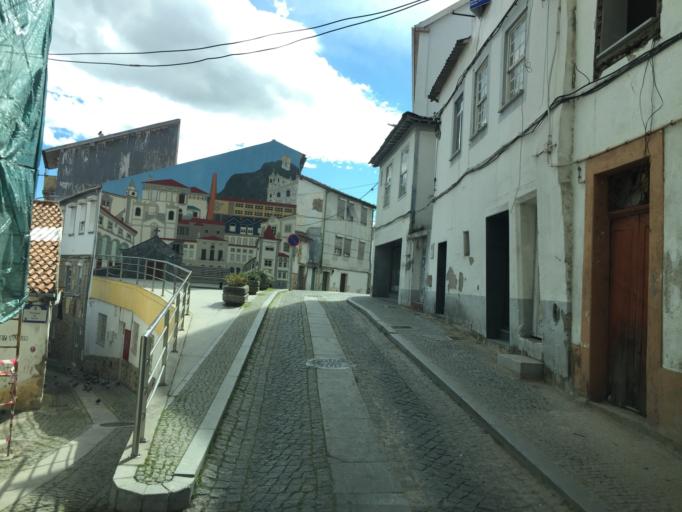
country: PT
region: Castelo Branco
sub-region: Covilha
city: Covilha
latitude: 40.2796
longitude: -7.5036
